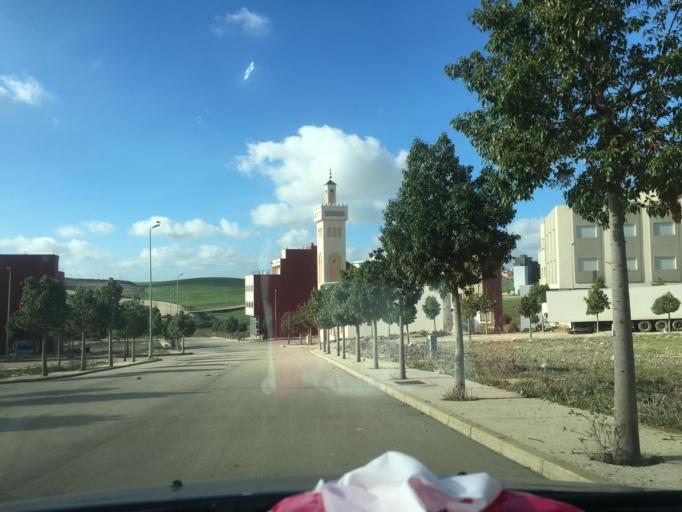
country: MA
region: Tanger-Tetouan
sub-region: Tanger-Assilah
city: Tangier
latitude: 35.7191
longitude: -5.8195
